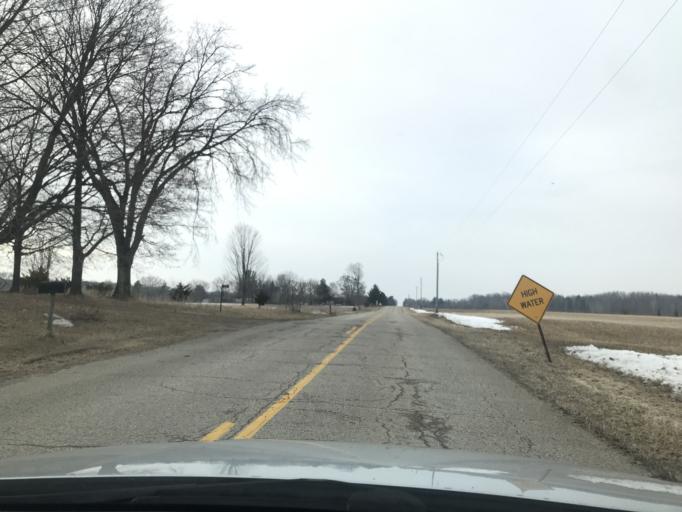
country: US
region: Wisconsin
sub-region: Oconto County
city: Oconto Falls
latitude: 44.8317
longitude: -88.1682
